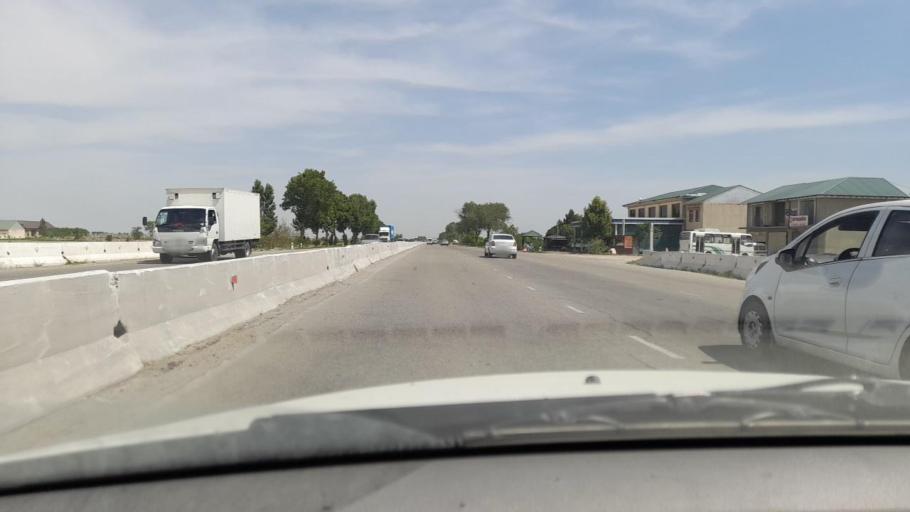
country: UZ
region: Bukhara
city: Galaosiyo
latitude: 39.8842
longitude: 64.4627
